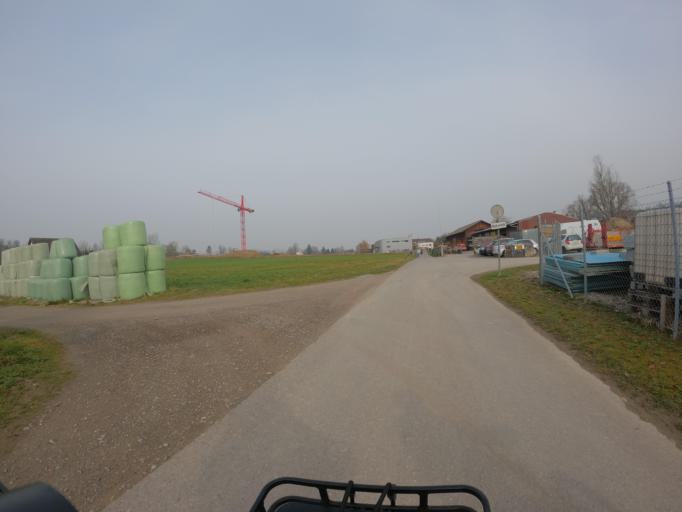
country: CH
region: Aargau
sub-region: Bezirk Bremgarten
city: Bremgarten
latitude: 47.3425
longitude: 8.3520
